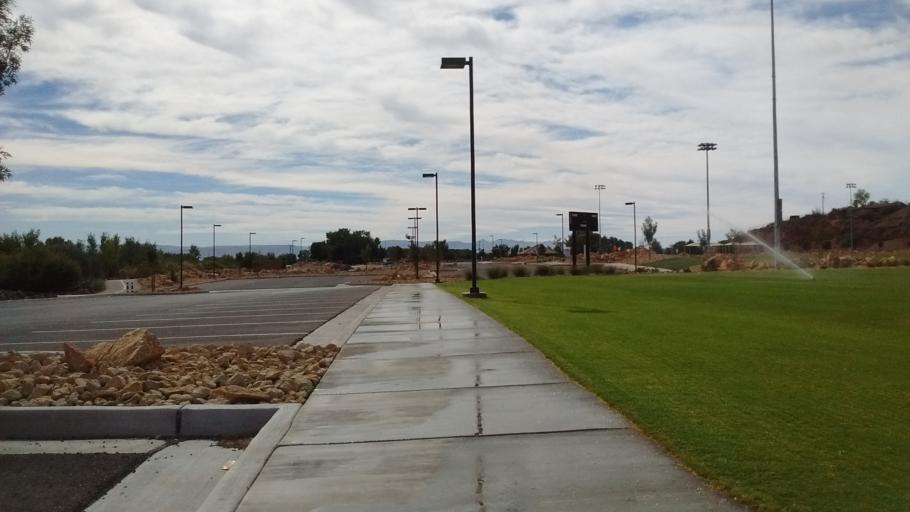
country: US
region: Utah
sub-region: Washington County
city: Washington
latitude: 37.1198
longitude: -113.4993
